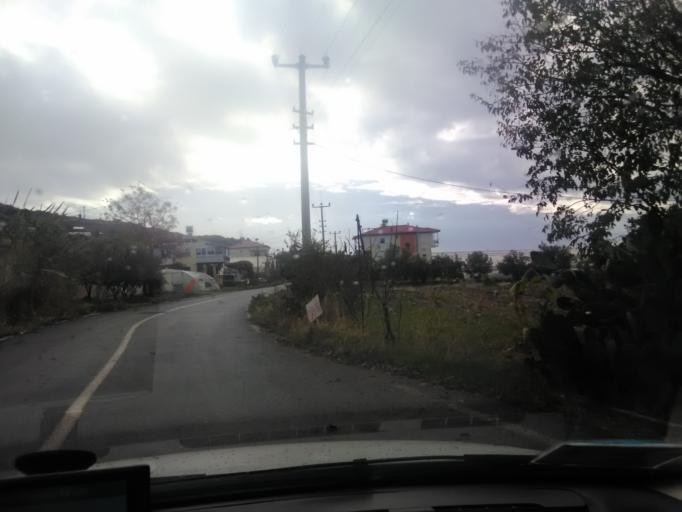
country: TR
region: Antalya
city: Gazipasa
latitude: 36.2440
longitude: 32.3013
